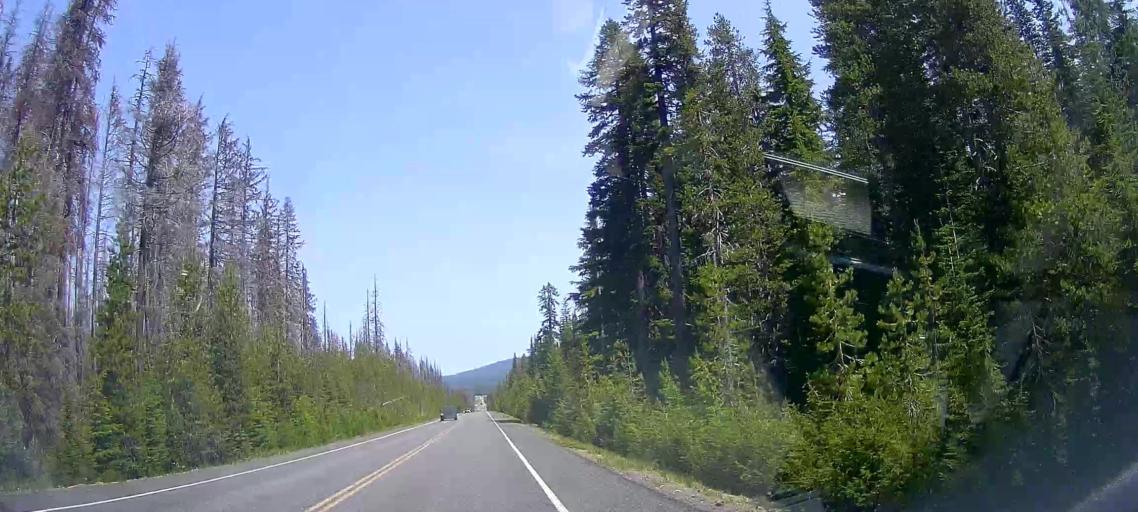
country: US
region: Oregon
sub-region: Lane County
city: Oakridge
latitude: 43.0691
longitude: -122.1194
